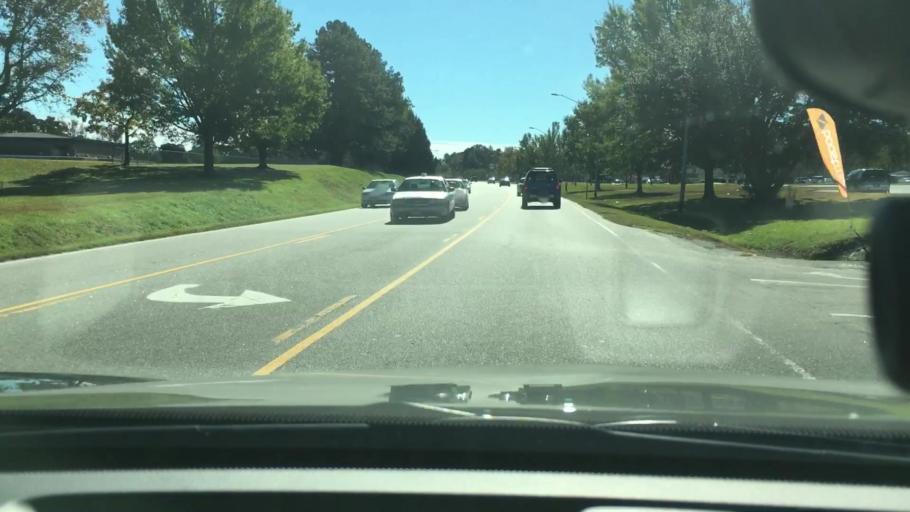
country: US
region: North Carolina
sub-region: Edgecombe County
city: Tarboro
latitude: 35.9028
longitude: -77.5618
